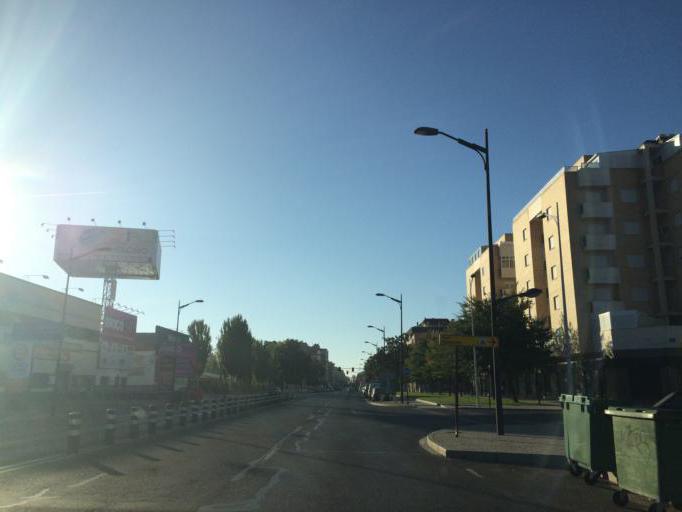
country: ES
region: Castille-La Mancha
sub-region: Provincia de Albacete
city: Albacete
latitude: 39.0093
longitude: -1.8725
